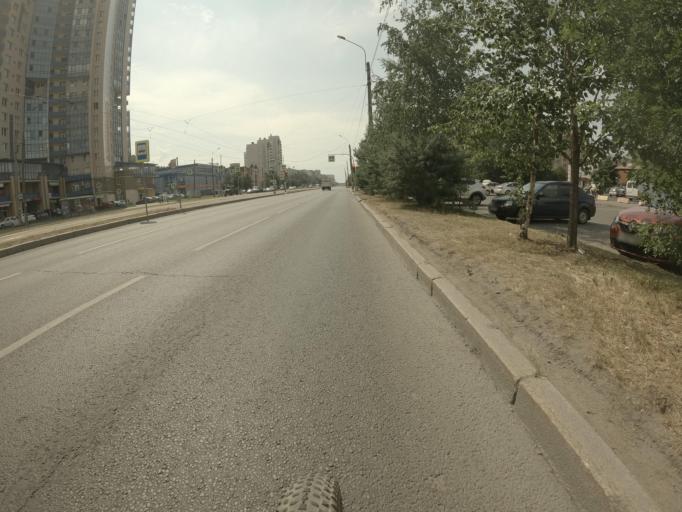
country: RU
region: St.-Petersburg
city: Krasnogvargeisky
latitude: 59.9234
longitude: 30.4849
